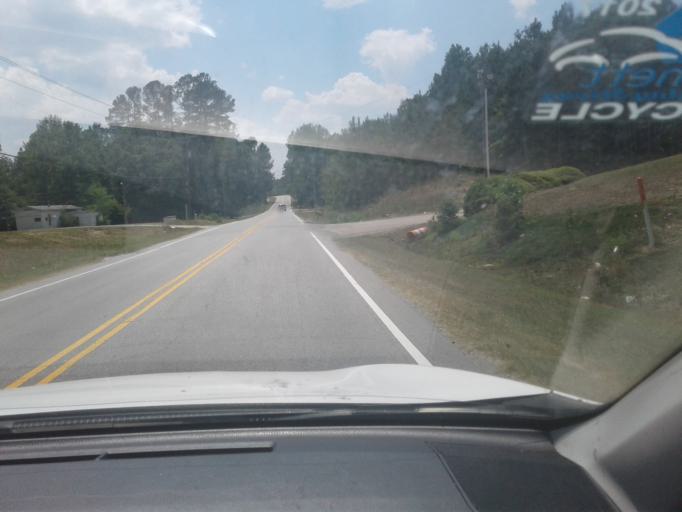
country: US
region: North Carolina
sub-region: Johnston County
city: Benson
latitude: 35.4203
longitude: -78.5346
